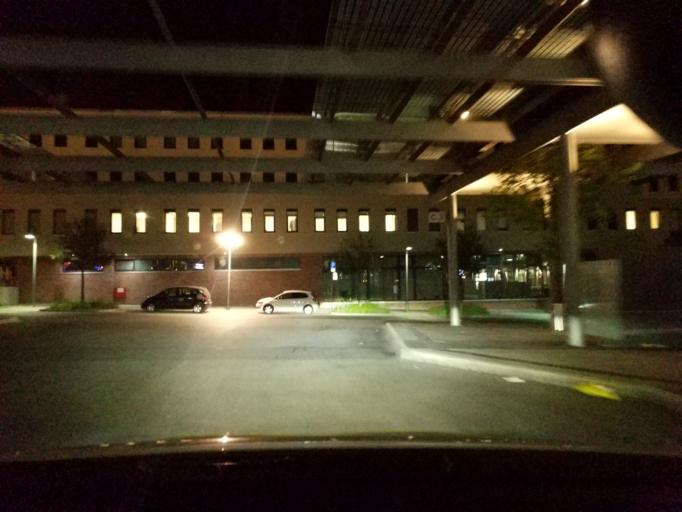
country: DE
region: Rheinland-Pfalz
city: Kaiserslautern
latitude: 49.4365
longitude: 7.7677
